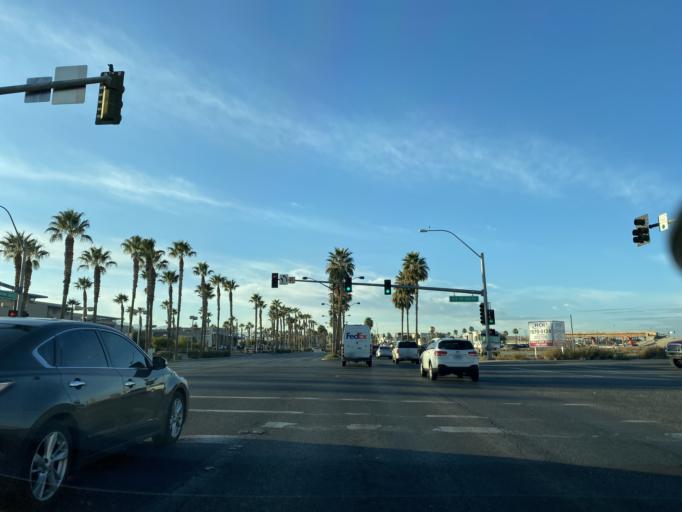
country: US
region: Nevada
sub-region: Clark County
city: Las Vegas
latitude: 36.2745
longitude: -115.2686
